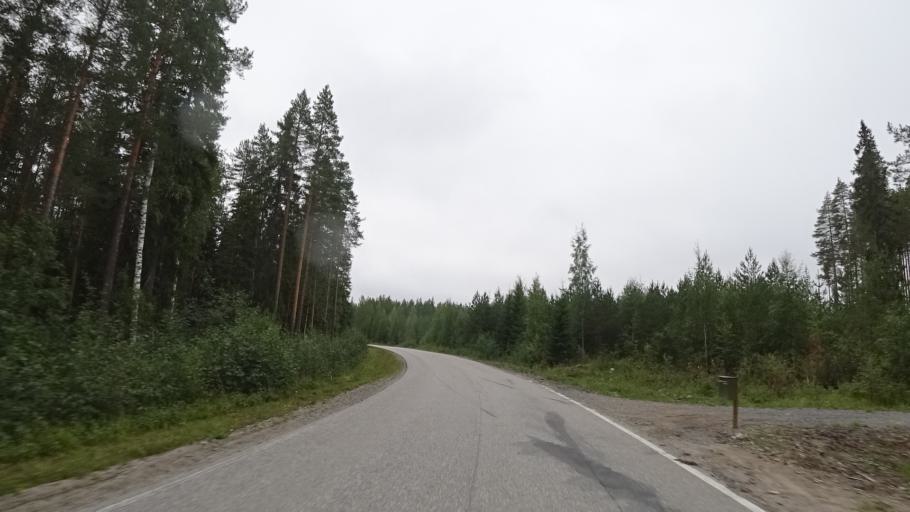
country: FI
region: North Karelia
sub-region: Pielisen Karjala
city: Lieksa
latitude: 63.3579
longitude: 30.2611
